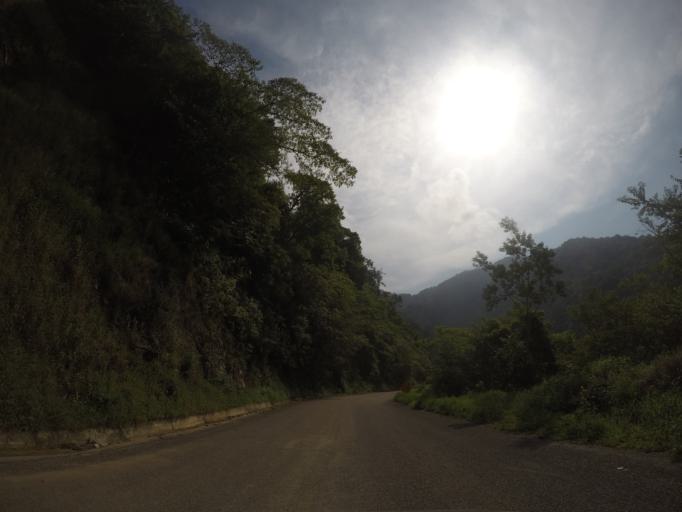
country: MX
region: Oaxaca
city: Pluma Hidalgo
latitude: 15.9381
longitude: -96.4355
